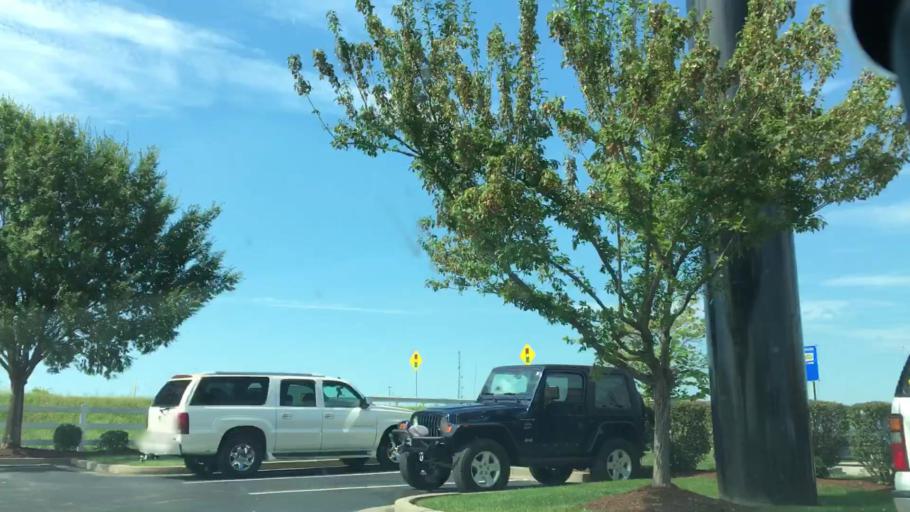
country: US
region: Kentucky
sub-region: Daviess County
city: Owensboro
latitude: 37.7551
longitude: -87.0707
